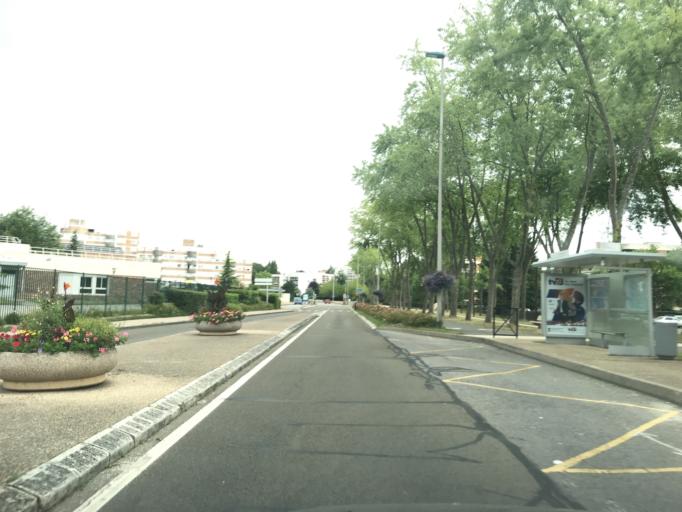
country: FR
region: Ile-de-France
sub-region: Departement des Yvelines
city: Elancourt
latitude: 48.7694
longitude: 1.9476
